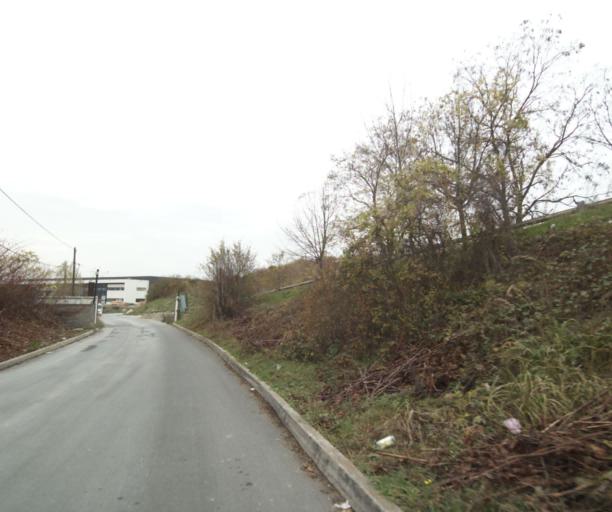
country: FR
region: Ile-de-France
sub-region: Departement de Seine-Saint-Denis
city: Le Blanc-Mesnil
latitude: 48.9650
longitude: 2.4656
